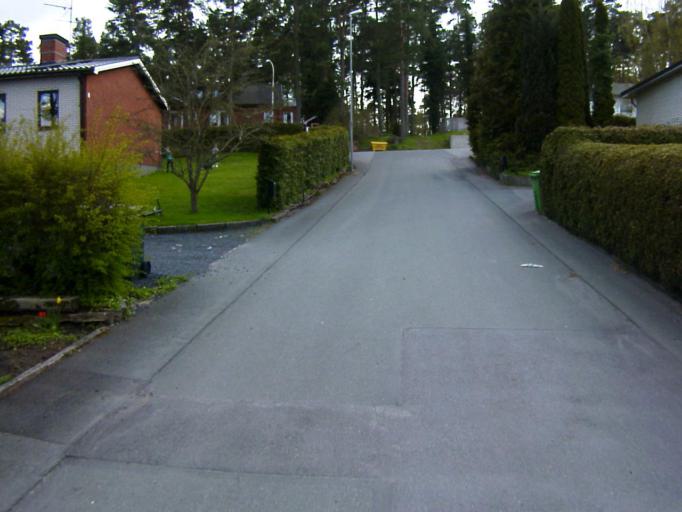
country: SE
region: Skane
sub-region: Kristianstads Kommun
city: Norra Asum
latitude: 55.9984
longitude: 14.0833
